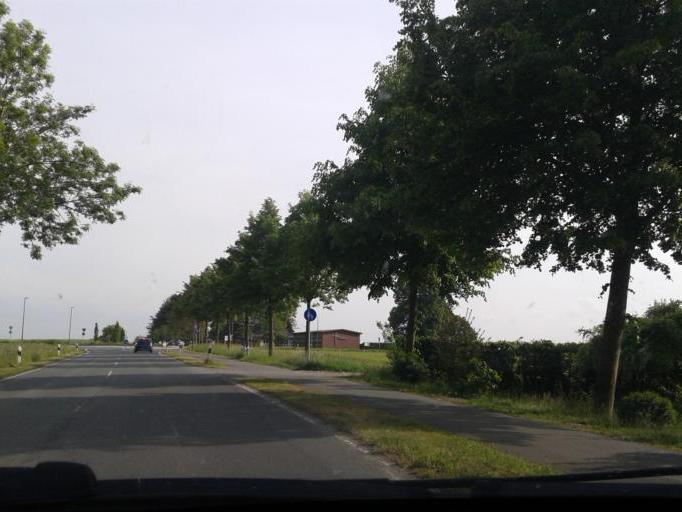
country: DE
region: North Rhine-Westphalia
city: Bad Lippspringe
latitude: 51.7739
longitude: 8.8193
